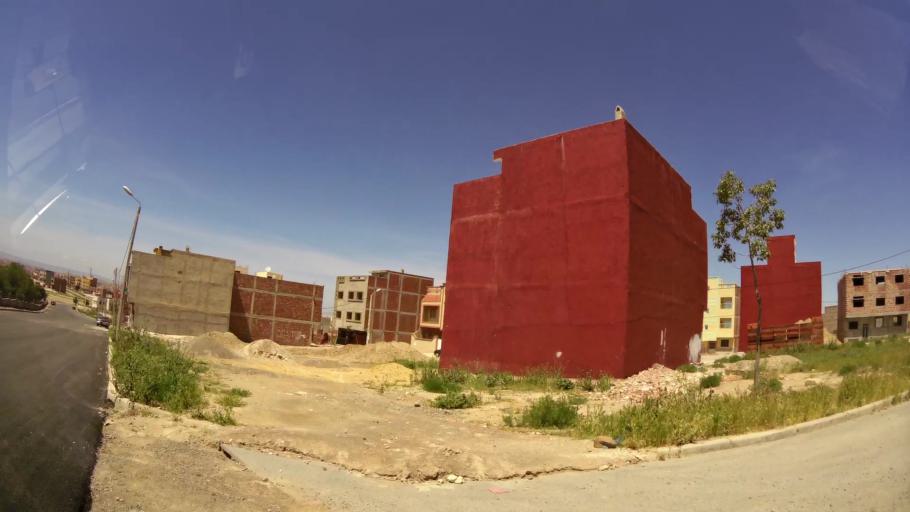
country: MA
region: Oriental
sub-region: Oujda-Angad
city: Oujda
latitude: 34.6522
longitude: -1.9224
